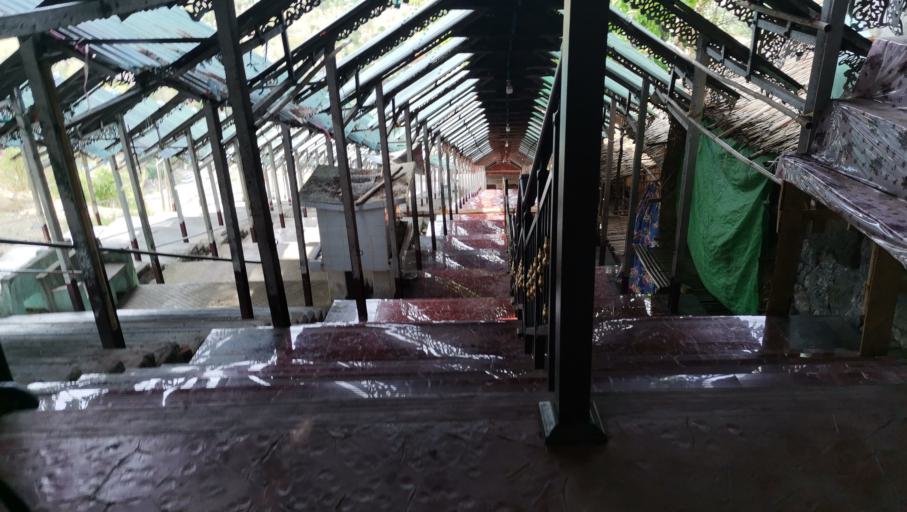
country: MM
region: Magway
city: Minbu
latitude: 20.1006
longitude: 94.5272
